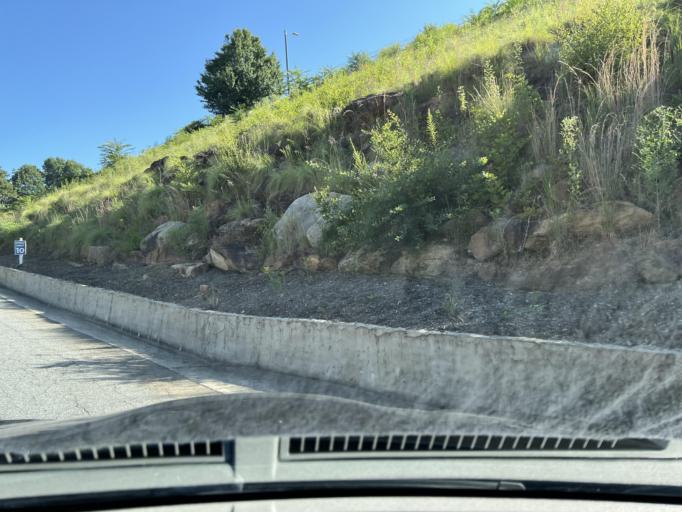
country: US
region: North Carolina
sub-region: Buncombe County
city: Woodfin
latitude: 35.6172
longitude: -82.5753
